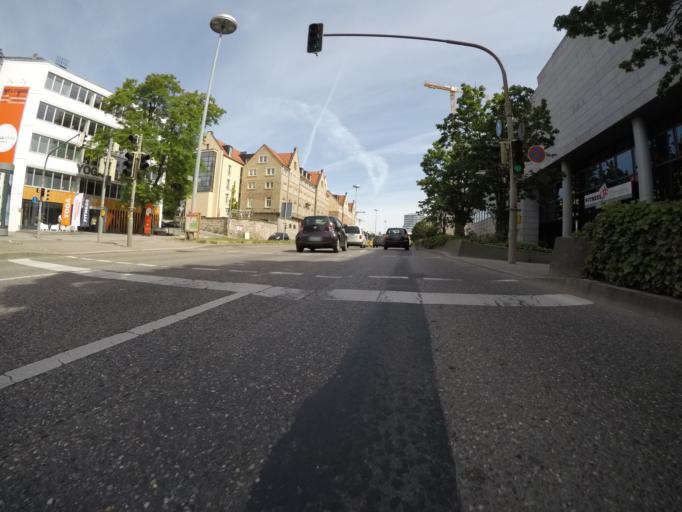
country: DE
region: Baden-Wuerttemberg
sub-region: Regierungsbezirk Stuttgart
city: Stuttgart
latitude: 48.7871
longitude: 9.1803
